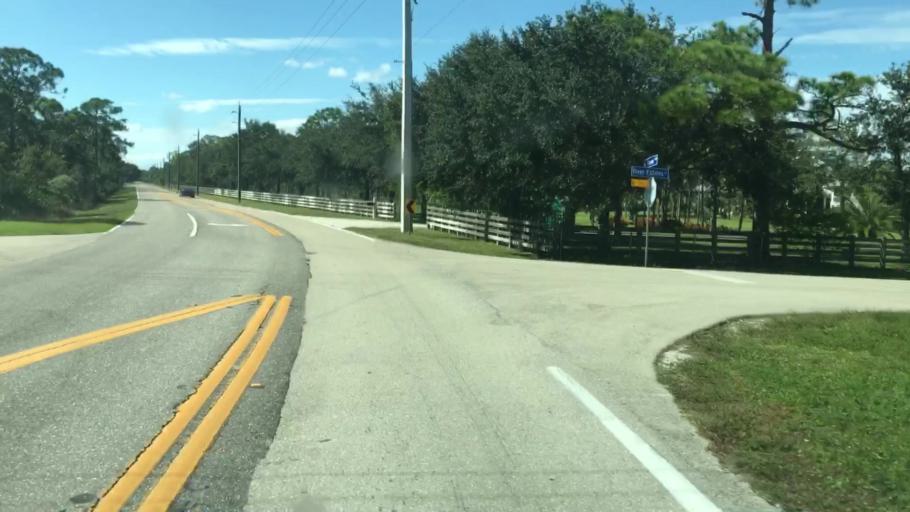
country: US
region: Florida
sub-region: Lee County
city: Olga
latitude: 26.7286
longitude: -81.6842
